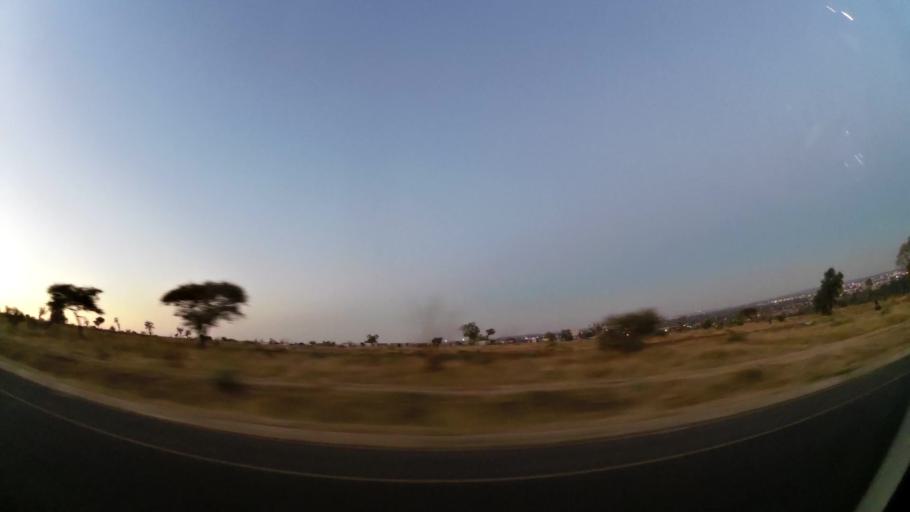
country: ZA
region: Limpopo
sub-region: Capricorn District Municipality
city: Polokwane
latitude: -23.8816
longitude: 29.4221
